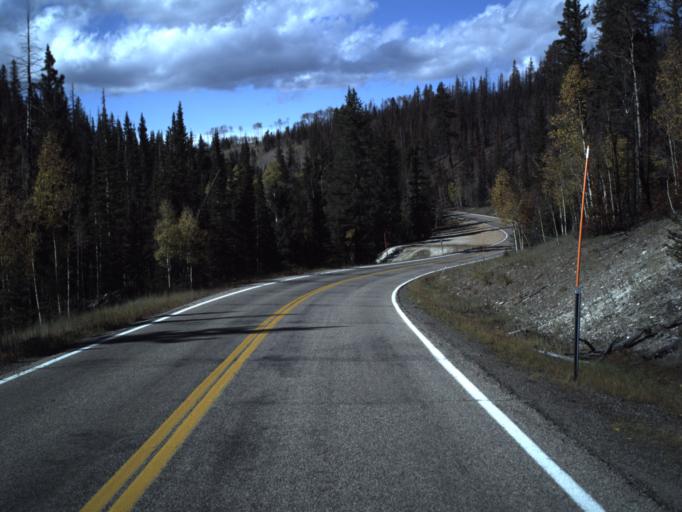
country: US
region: Utah
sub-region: Iron County
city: Parowan
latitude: 37.6569
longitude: -112.7153
